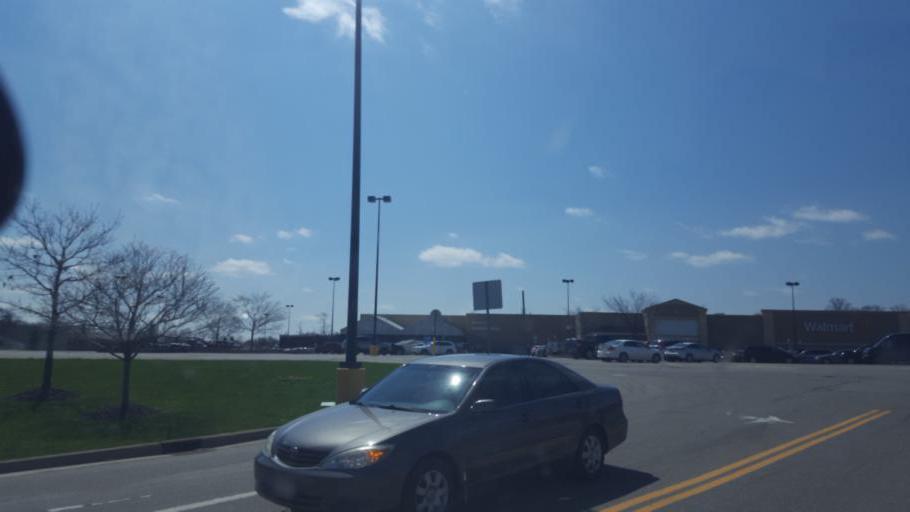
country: US
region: Ohio
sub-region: Geauga County
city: Middlefield
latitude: 41.4604
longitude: -81.0848
